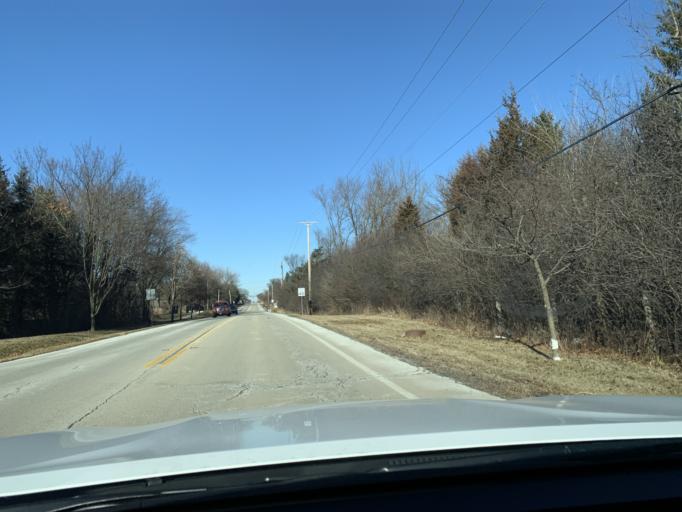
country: US
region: Illinois
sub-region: DuPage County
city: Burr Ridge
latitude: 41.7336
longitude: -87.9149
